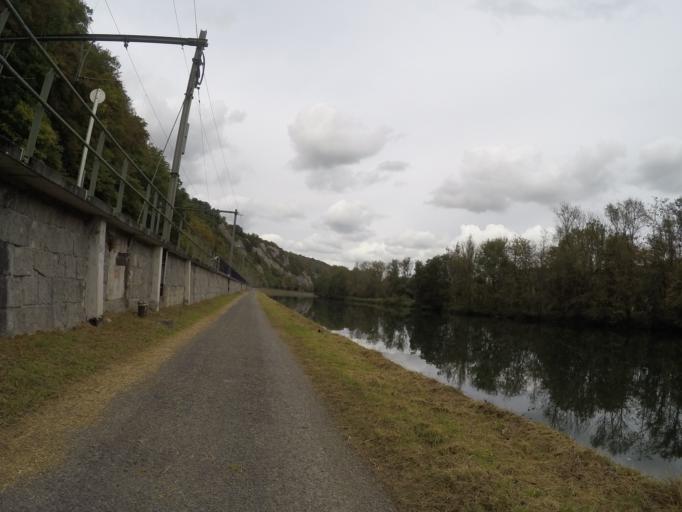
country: BE
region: Wallonia
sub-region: Province de Namur
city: Anhee
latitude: 50.2831
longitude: 4.8916
